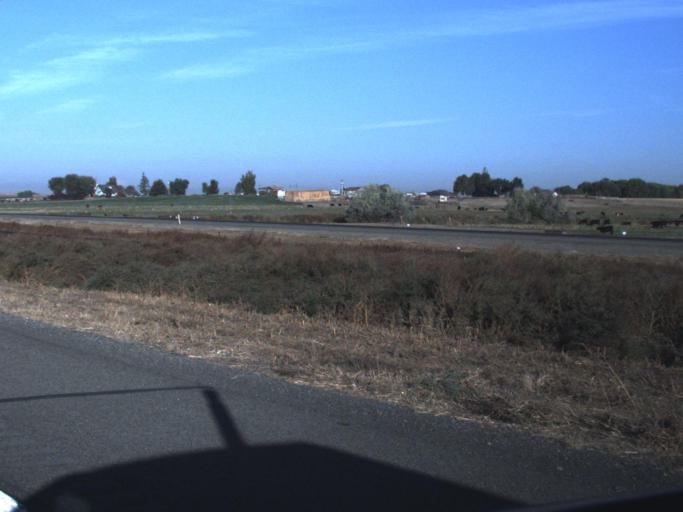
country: US
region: Washington
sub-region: Yakima County
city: Granger
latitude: 46.3386
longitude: -120.1394
